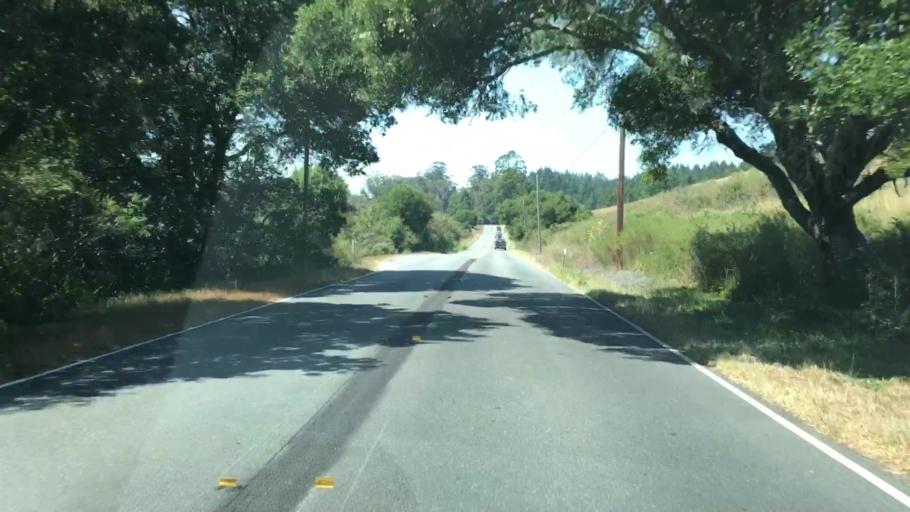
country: US
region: California
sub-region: Marin County
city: Lagunitas-Forest Knolls
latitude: 37.9647
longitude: -122.7231
